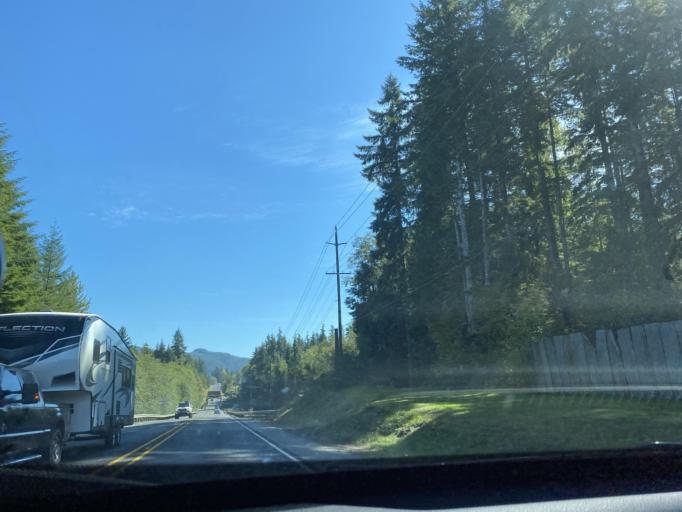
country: US
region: Washington
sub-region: Clallam County
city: Forks
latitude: 47.9618
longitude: -124.3971
